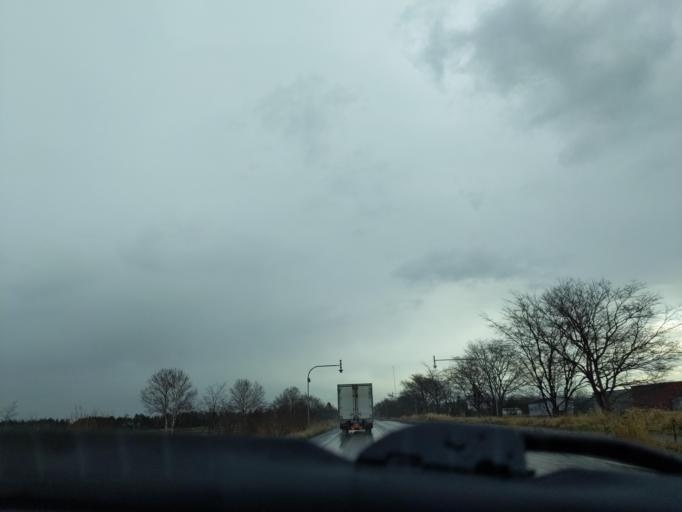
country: JP
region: Hokkaido
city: Ebetsu
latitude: 43.1096
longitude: 141.5921
